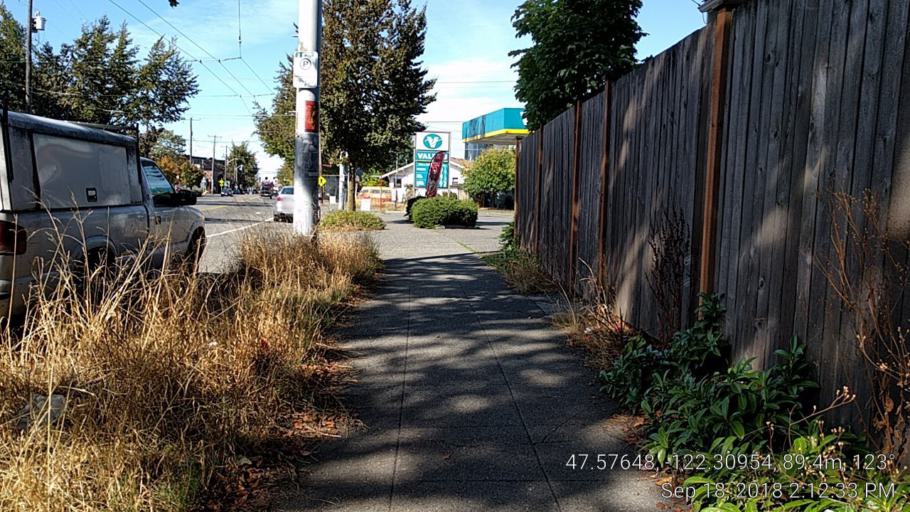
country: US
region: Washington
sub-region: King County
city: Seattle
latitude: 47.5765
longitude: -122.3096
